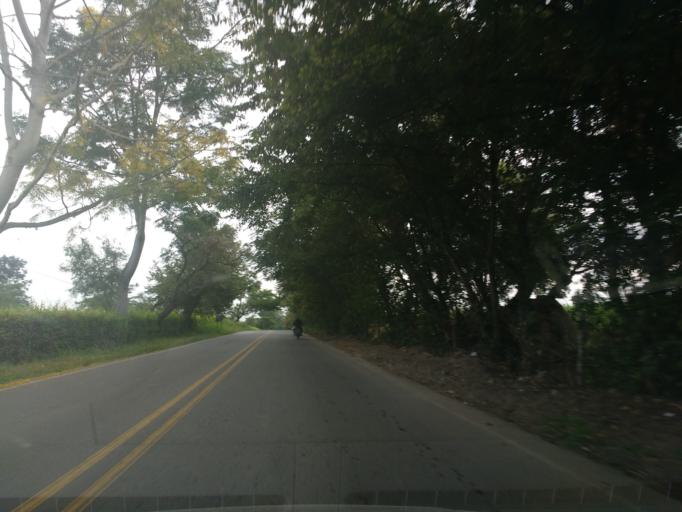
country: CO
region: Valle del Cauca
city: Florida
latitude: 3.3000
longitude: -76.2312
